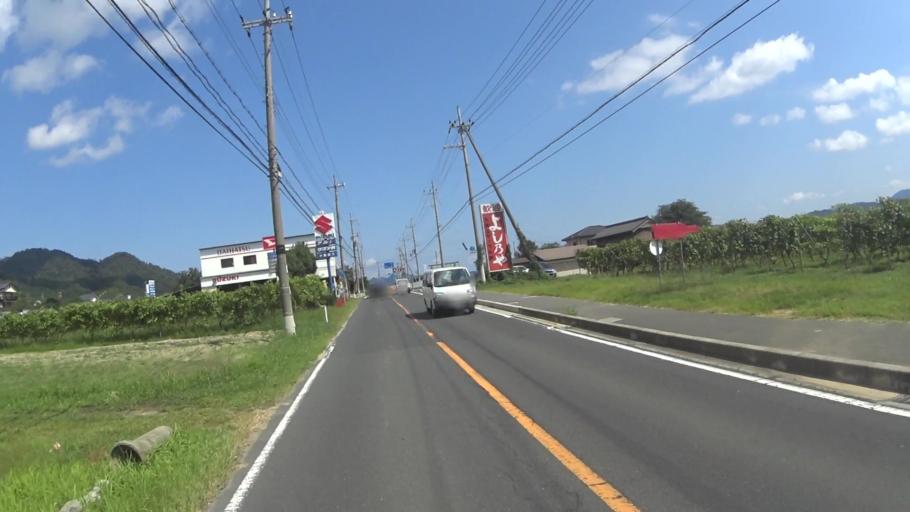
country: JP
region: Kyoto
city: Miyazu
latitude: 35.5761
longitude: 135.1778
